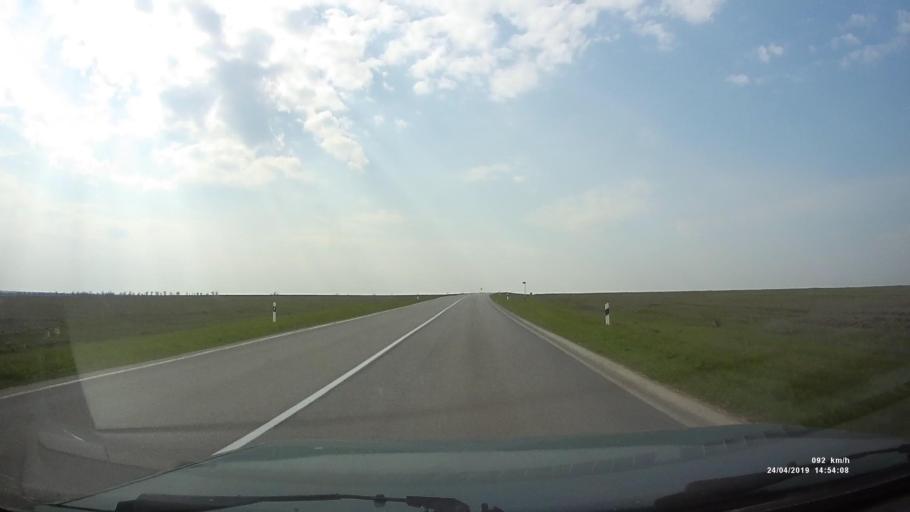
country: RU
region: Rostov
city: Remontnoye
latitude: 46.5327
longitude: 43.6445
